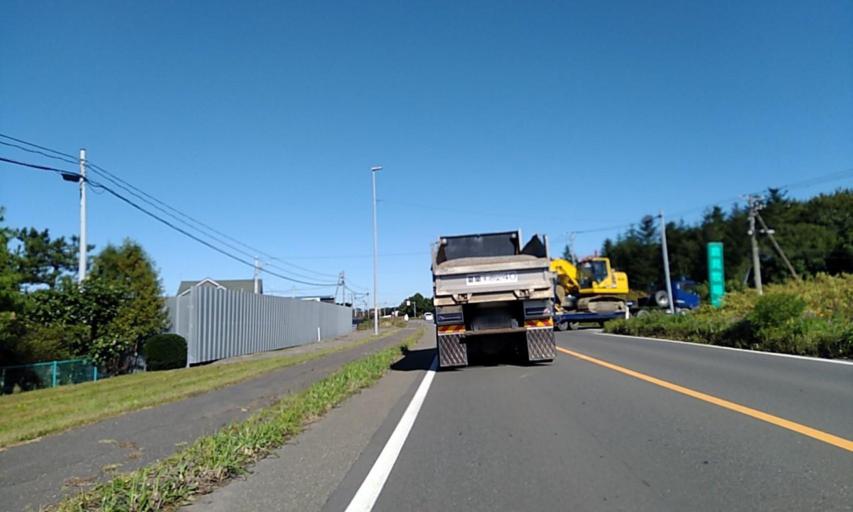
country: JP
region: Hokkaido
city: Shizunai-furukawacho
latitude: 42.4943
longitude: 142.0557
